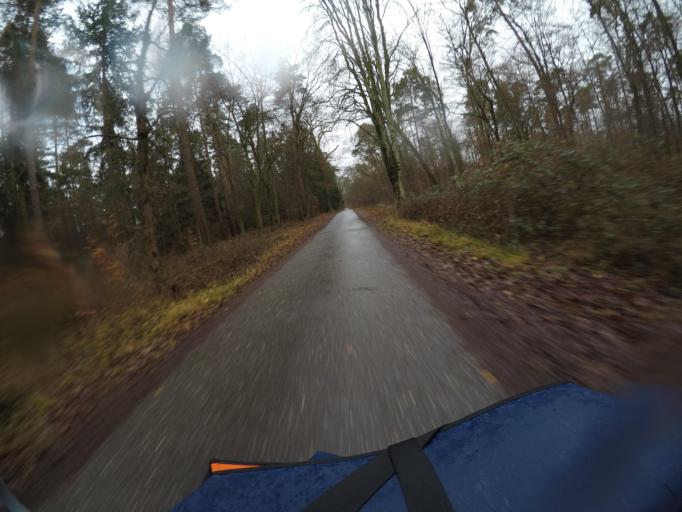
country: DE
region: Baden-Wuerttemberg
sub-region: Karlsruhe Region
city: Eggenstein-Leopoldshafen
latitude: 49.0785
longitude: 8.4530
